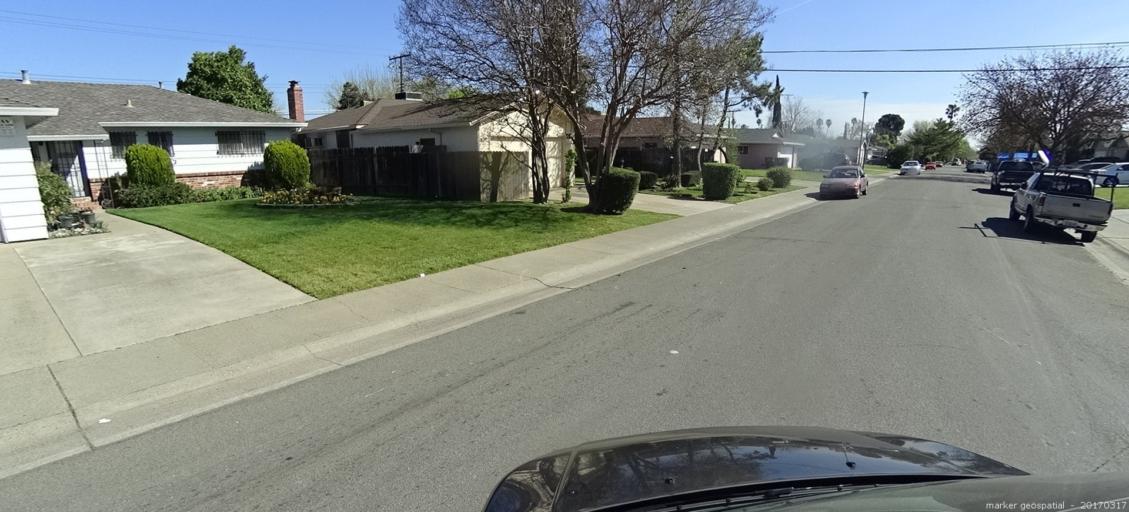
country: US
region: California
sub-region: Sacramento County
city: Parkway
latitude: 38.4882
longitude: -121.4949
